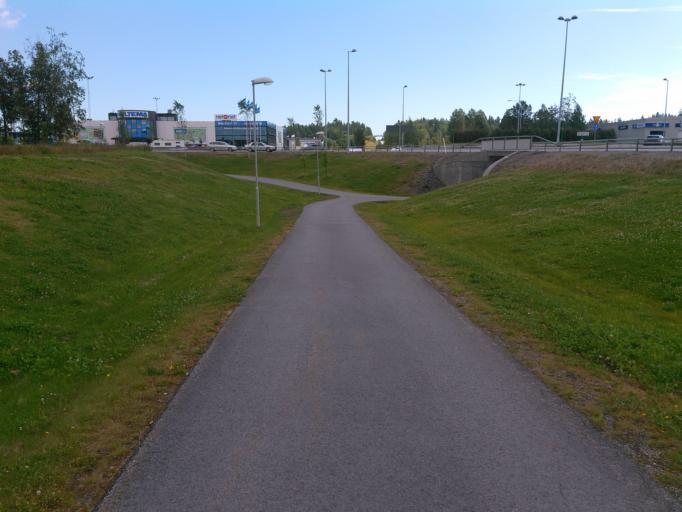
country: SE
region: Vaesterbotten
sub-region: Umea Kommun
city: Ersmark
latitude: 63.8487
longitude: 20.3125
